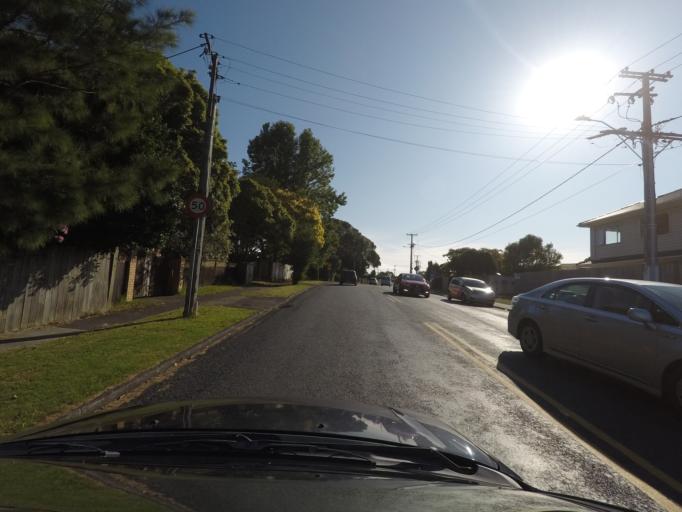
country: NZ
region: Auckland
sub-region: Auckland
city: Rosebank
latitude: -36.8622
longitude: 174.6127
